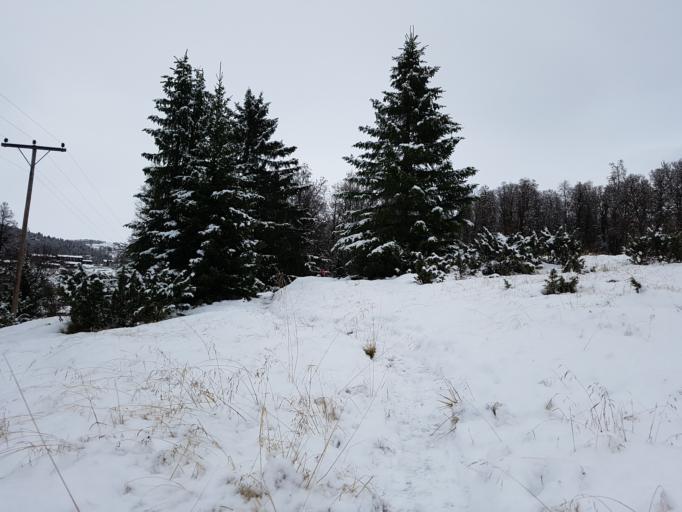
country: NO
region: Oppland
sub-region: Sel
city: Otta
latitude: 61.8077
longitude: 9.6780
